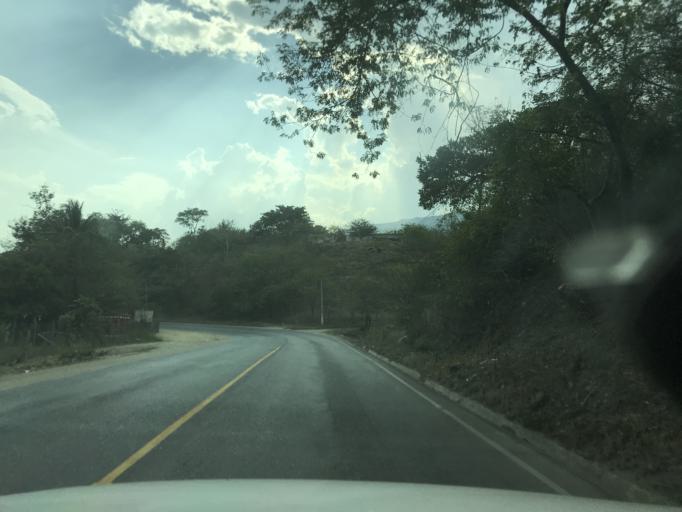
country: GT
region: Zacapa
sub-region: Municipio de Zacapa
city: Gualan
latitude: 15.1817
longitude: -89.3014
